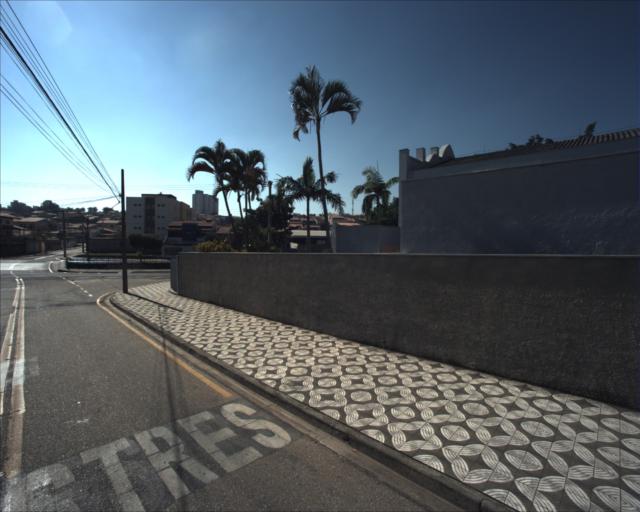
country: BR
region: Sao Paulo
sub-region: Sorocaba
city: Sorocaba
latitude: -23.5097
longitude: -47.4325
